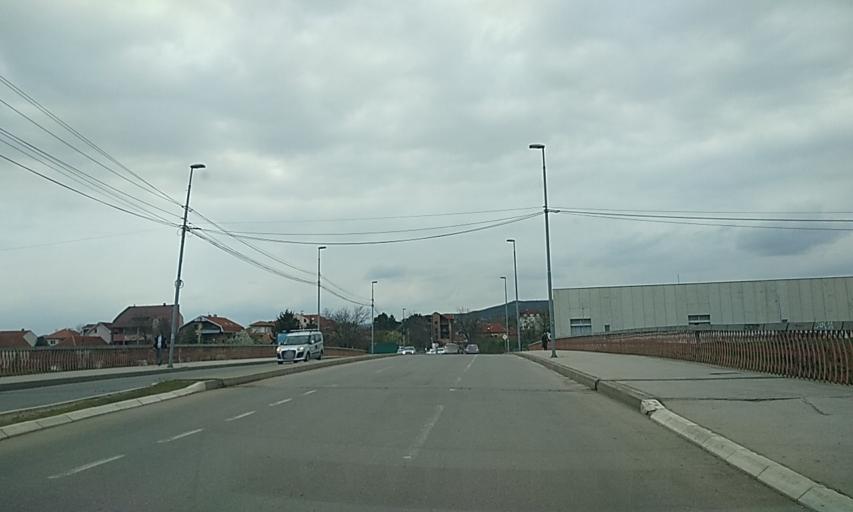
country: RS
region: Central Serbia
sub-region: Nisavski Okrug
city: Nis
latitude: 43.3260
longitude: 21.9090
